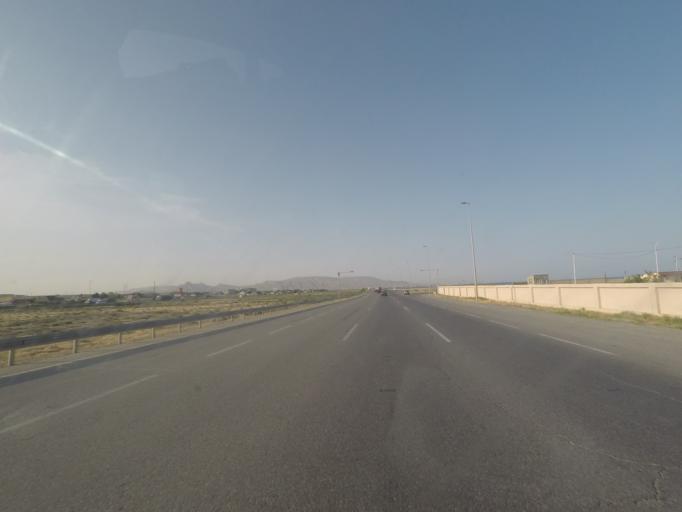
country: AZ
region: Baki
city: Qobustan
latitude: 40.1575
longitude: 49.4612
